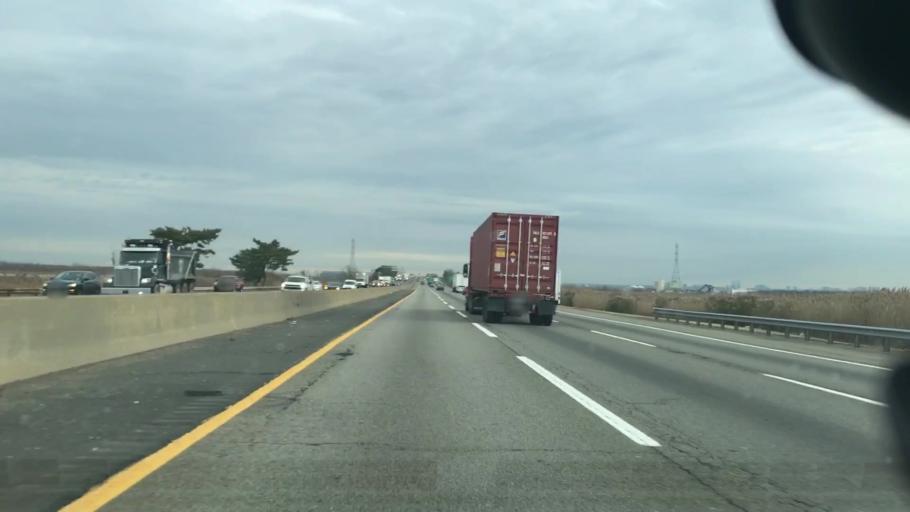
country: US
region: New Jersey
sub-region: Bergen County
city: North Arlington
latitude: 40.7763
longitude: -74.1011
